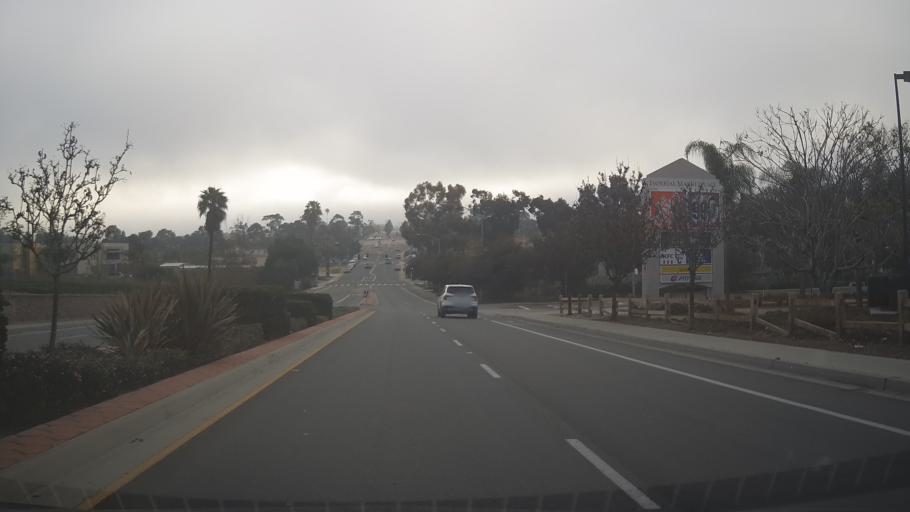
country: US
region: California
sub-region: San Diego County
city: National City
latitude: 32.7041
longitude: -117.1002
